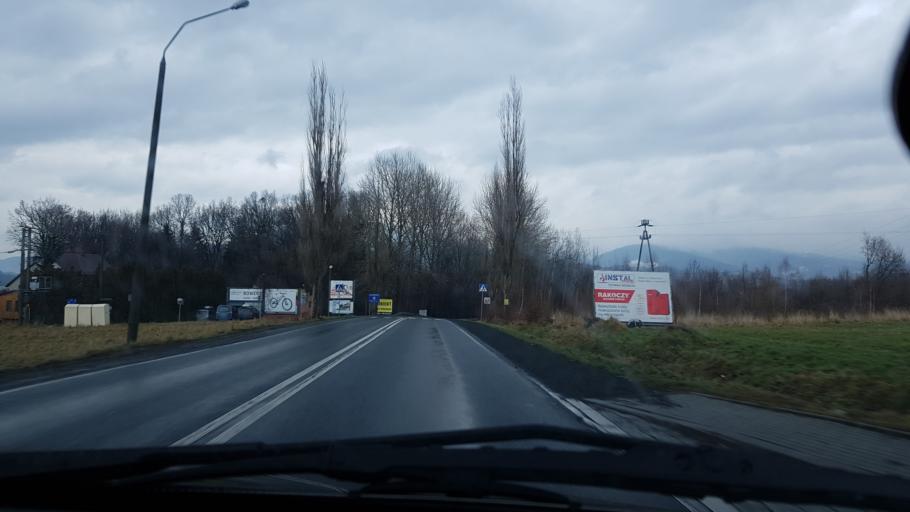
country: PL
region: Silesian Voivodeship
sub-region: Powiat zywiecki
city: Zywiec
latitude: 49.7077
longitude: 19.2094
